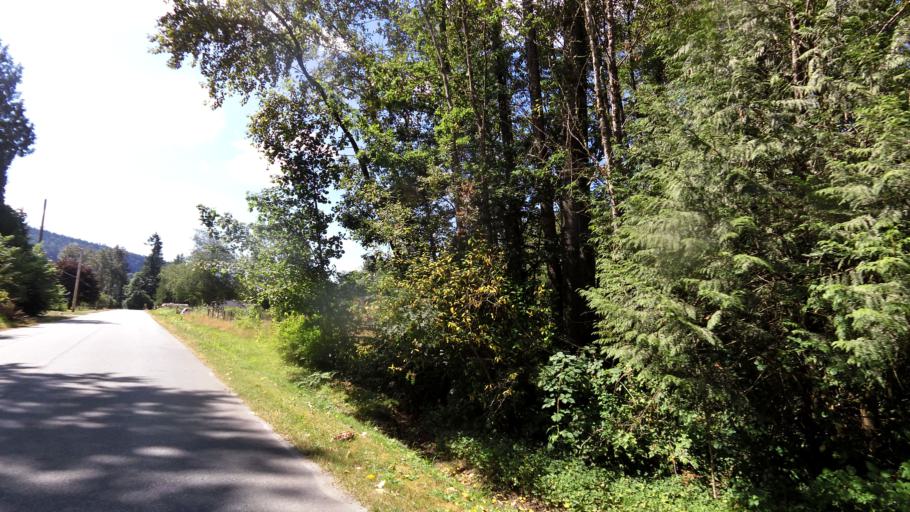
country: CA
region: British Columbia
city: Maple Ridge
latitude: 49.2184
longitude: -122.5237
